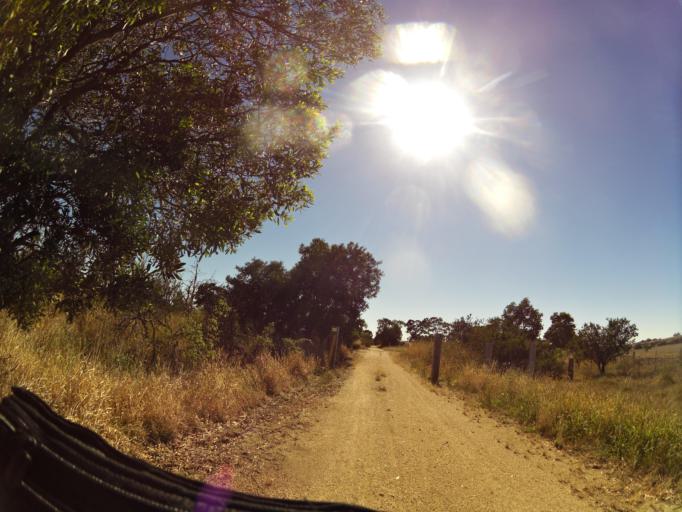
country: AU
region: Victoria
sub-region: Ballarat North
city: Delacombe
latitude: -37.6837
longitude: 143.4175
